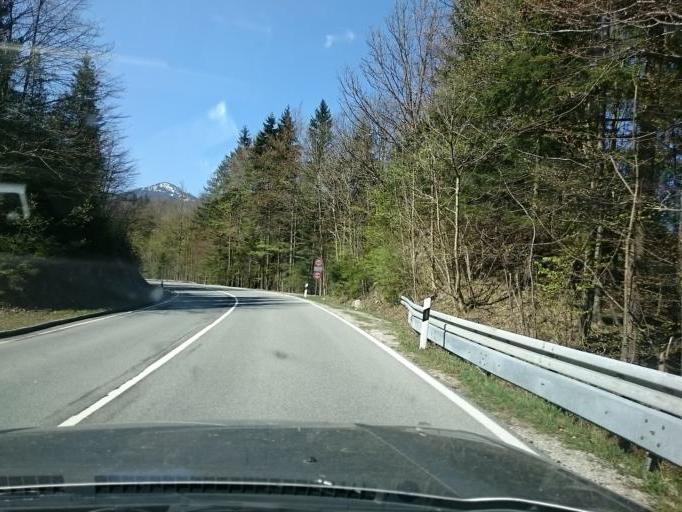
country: DE
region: Bavaria
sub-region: Upper Bavaria
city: Kochel
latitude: 47.6254
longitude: 11.3540
